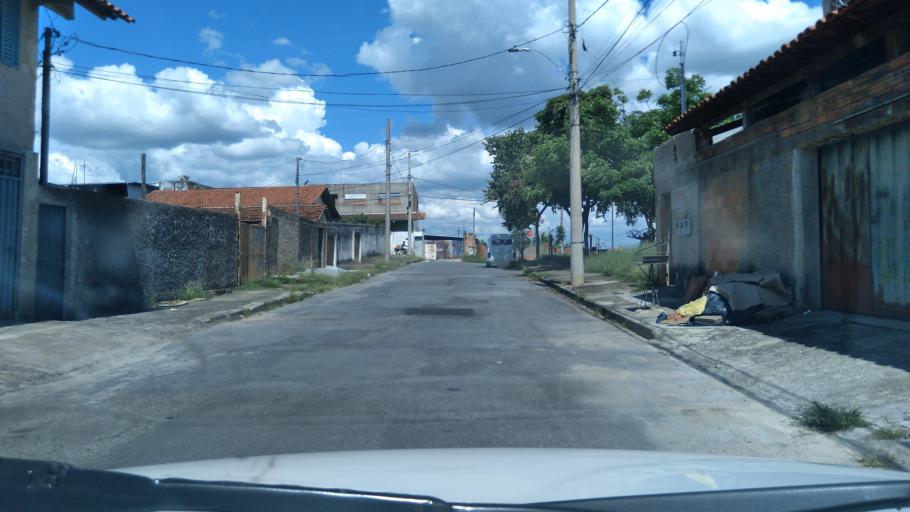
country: BR
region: Minas Gerais
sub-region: Belo Horizonte
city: Belo Horizonte
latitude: -19.8669
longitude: -43.9156
